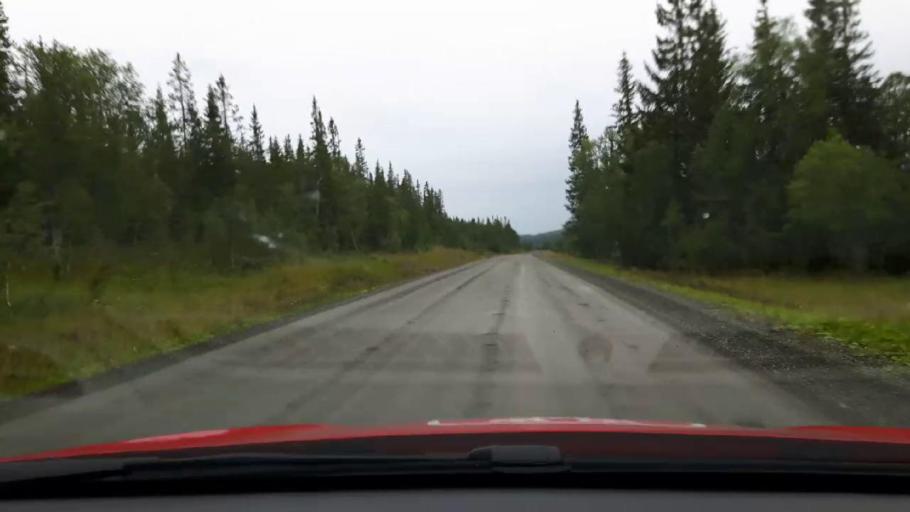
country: NO
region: Nord-Trondelag
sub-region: Meraker
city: Meraker
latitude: 63.5413
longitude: 12.3807
